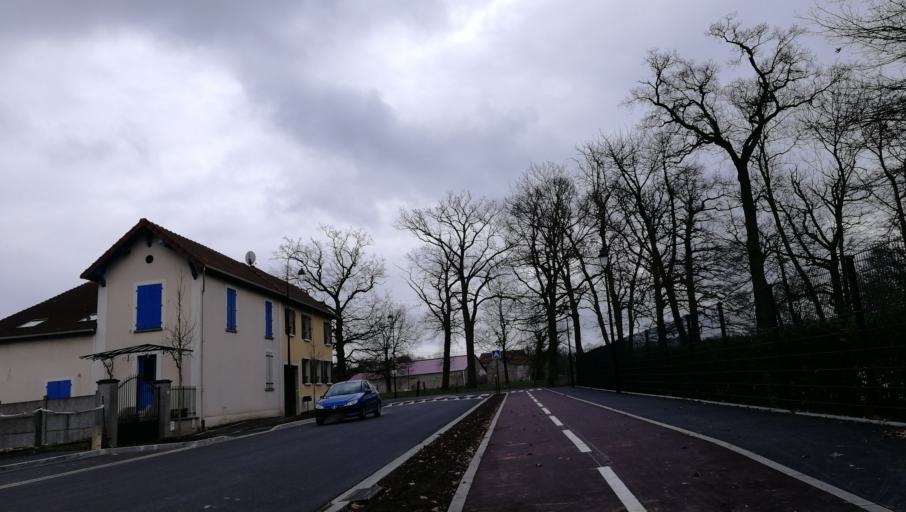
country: FR
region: Ile-de-France
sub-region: Departement du Val-de-Marne
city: Le Plessis-Trevise
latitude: 48.8036
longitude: 2.5803
